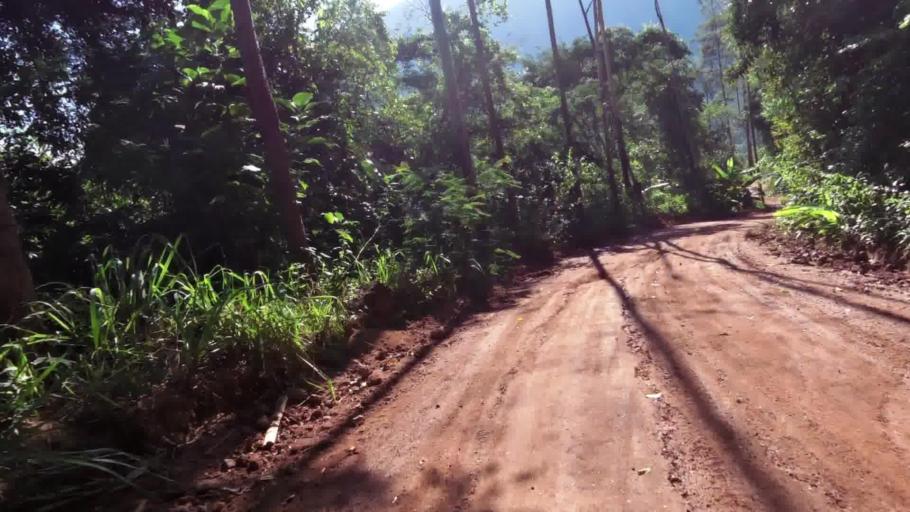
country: BR
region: Espirito Santo
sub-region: Alfredo Chaves
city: Alfredo Chaves
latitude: -20.6067
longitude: -40.7621
